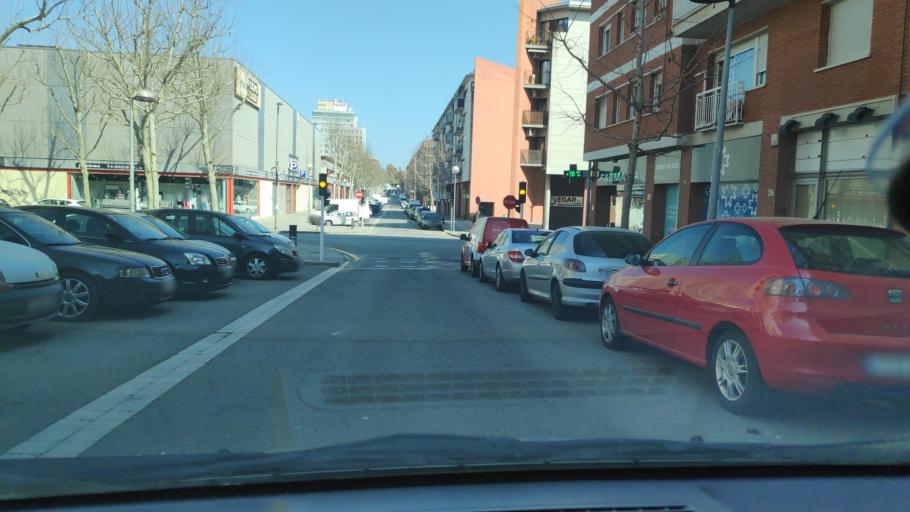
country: ES
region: Catalonia
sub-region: Provincia de Barcelona
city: Mollet del Valles
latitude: 41.5476
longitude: 2.2029
